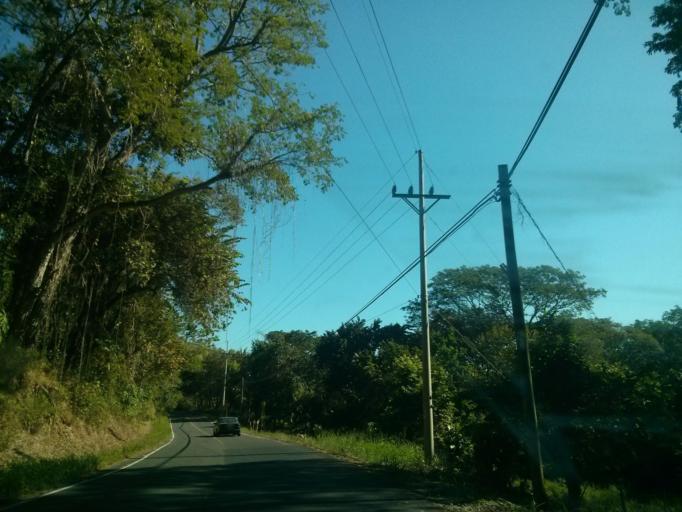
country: CR
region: Puntarenas
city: Paquera
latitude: 9.7550
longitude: -84.9921
